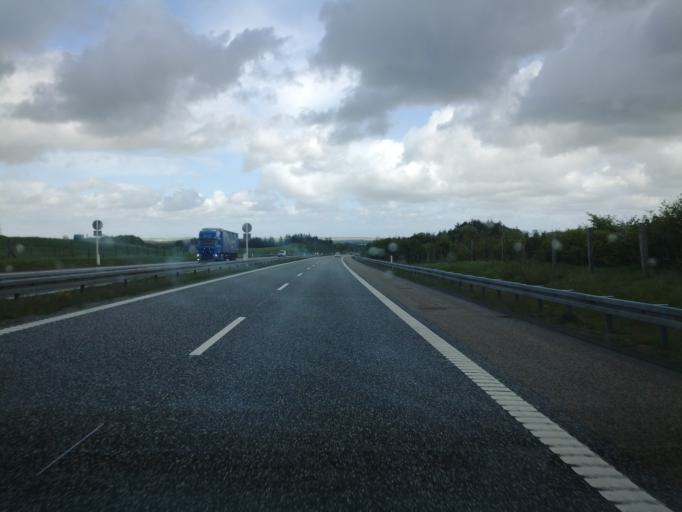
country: DK
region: North Denmark
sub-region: Bronderslev Kommune
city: Dronninglund
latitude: 57.2355
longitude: 10.2462
